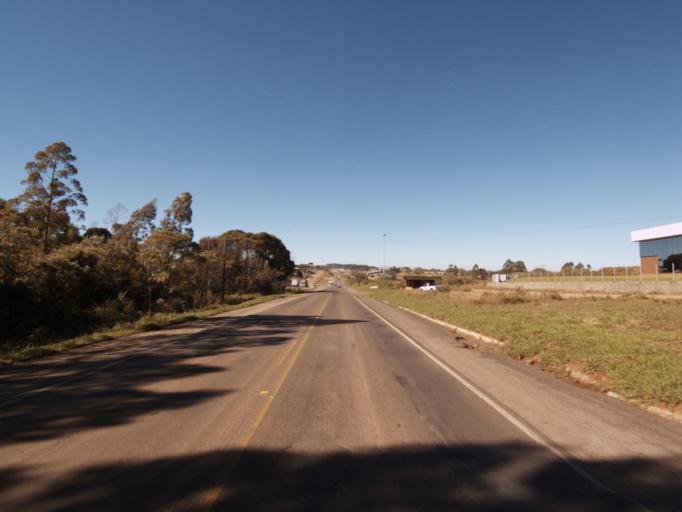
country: BR
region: Santa Catarina
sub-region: Sao Lourenco Do Oeste
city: Sao Lourenco dOeste
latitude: -26.7696
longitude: -53.2101
